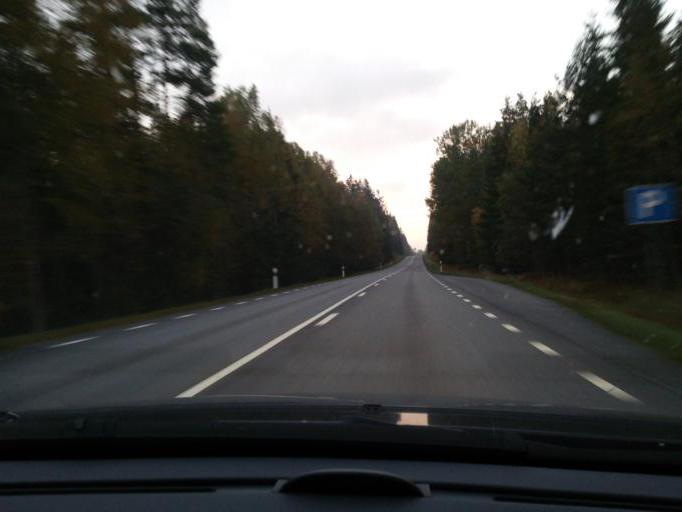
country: SE
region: Kronoberg
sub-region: Vaxjo Kommun
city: Lammhult
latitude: 57.1260
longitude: 14.6277
